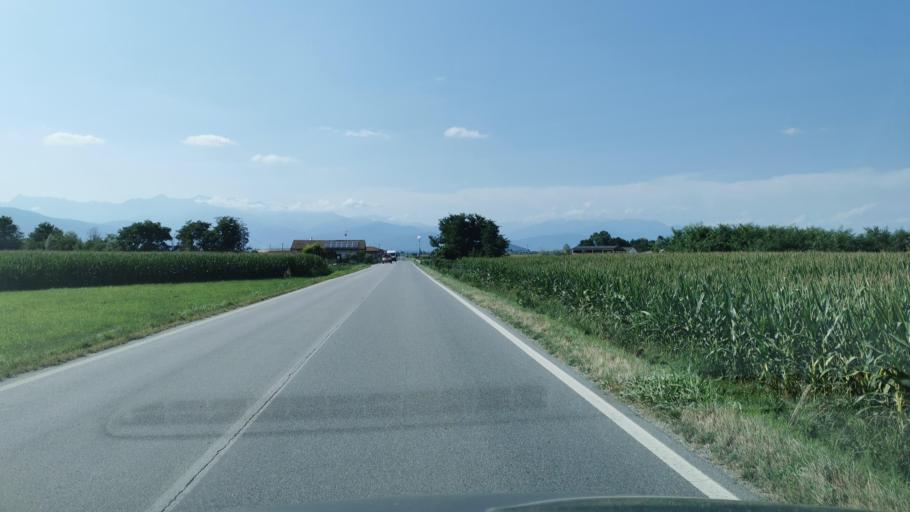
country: IT
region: Piedmont
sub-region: Provincia di Cuneo
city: Carde
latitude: 44.7263
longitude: 7.4327
